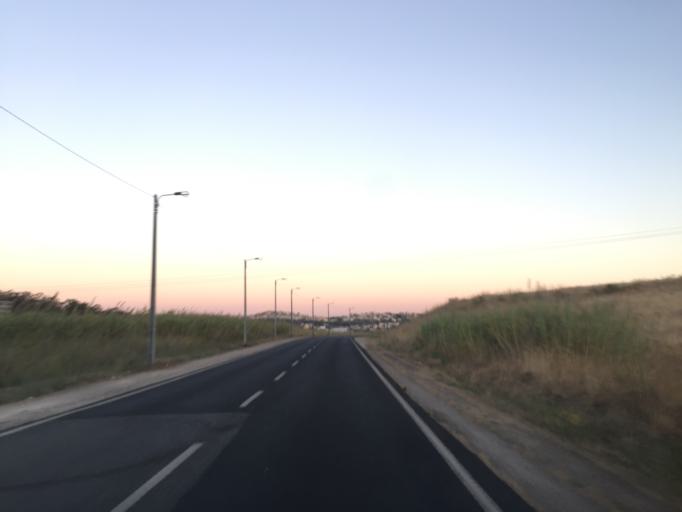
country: PT
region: Lisbon
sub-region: Odivelas
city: Povoa de Santo Adriao
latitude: 38.8099
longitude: -9.1724
